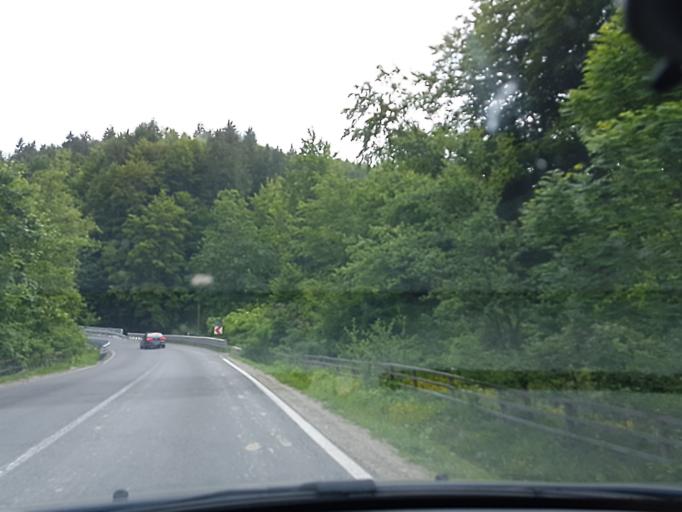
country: RO
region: Prahova
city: Maneciu
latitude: 45.3653
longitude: 25.9309
